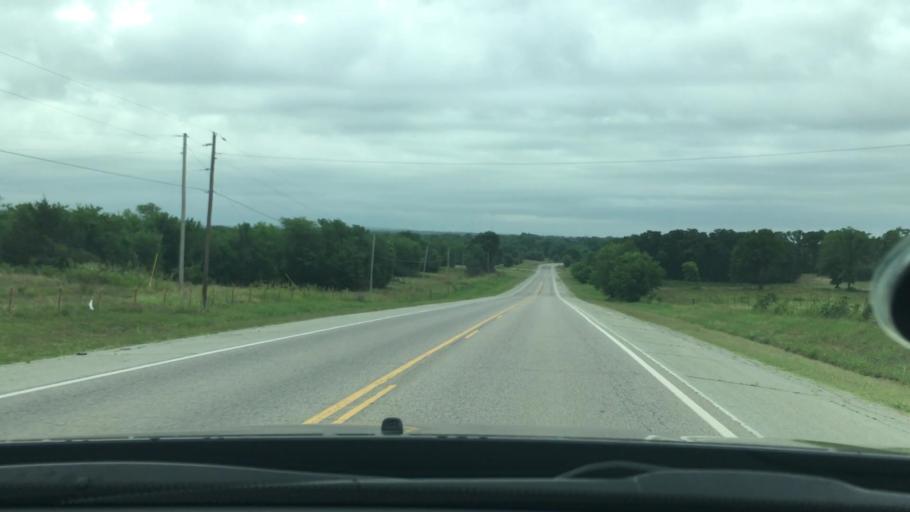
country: US
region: Oklahoma
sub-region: Coal County
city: Coalgate
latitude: 34.5528
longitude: -96.2370
